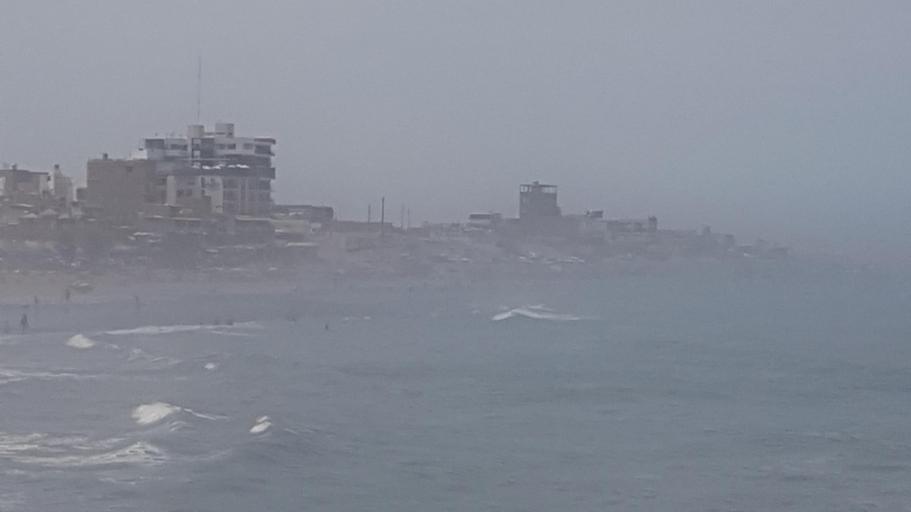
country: PE
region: Lambayeque
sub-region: Provincia de Chiclayo
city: Pimentel
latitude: -6.8372
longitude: -79.9392
